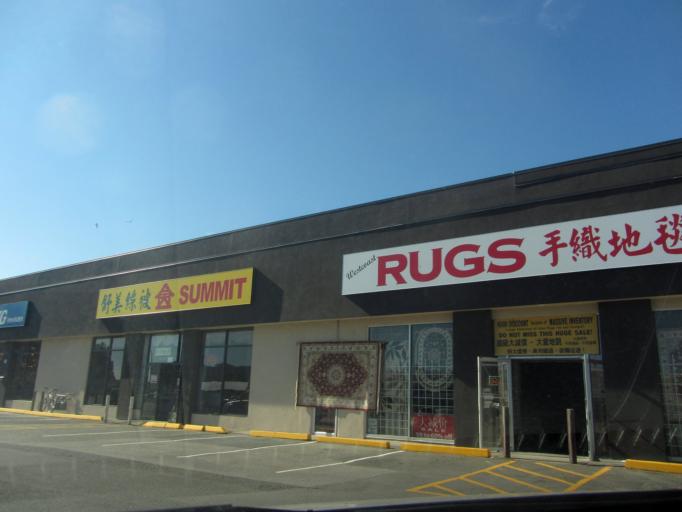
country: CA
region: British Columbia
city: Richmond
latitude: 49.1775
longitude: -123.1372
